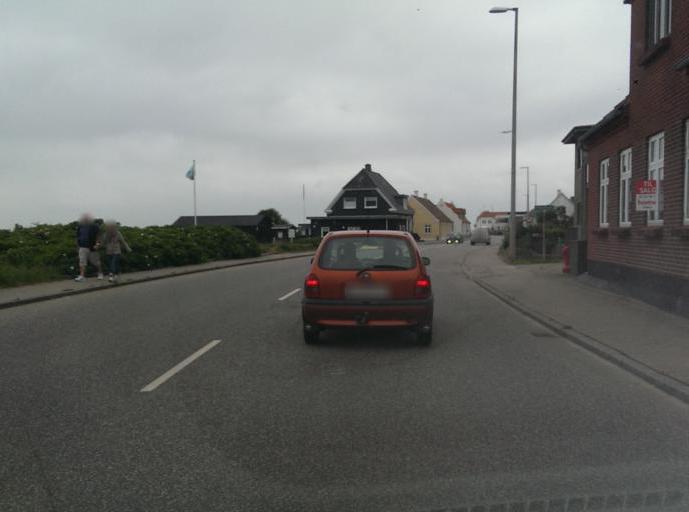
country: DK
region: South Denmark
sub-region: Fano Kommune
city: Nordby
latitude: 55.5213
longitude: 8.3572
